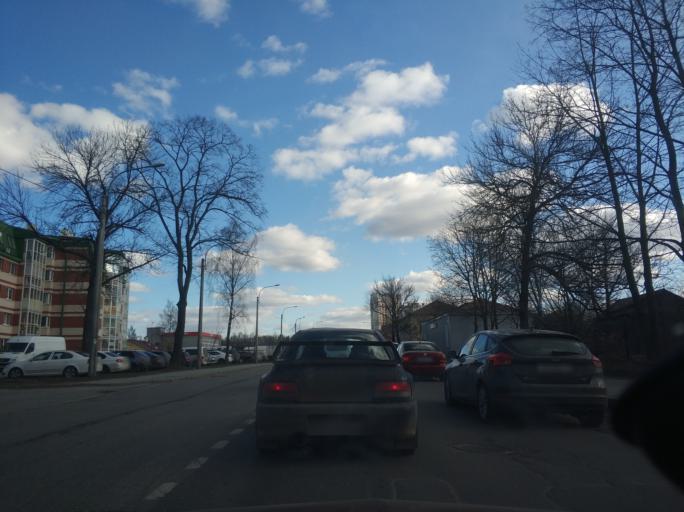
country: RU
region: St.-Petersburg
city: Krasnogvargeisky
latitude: 59.9647
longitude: 30.4857
